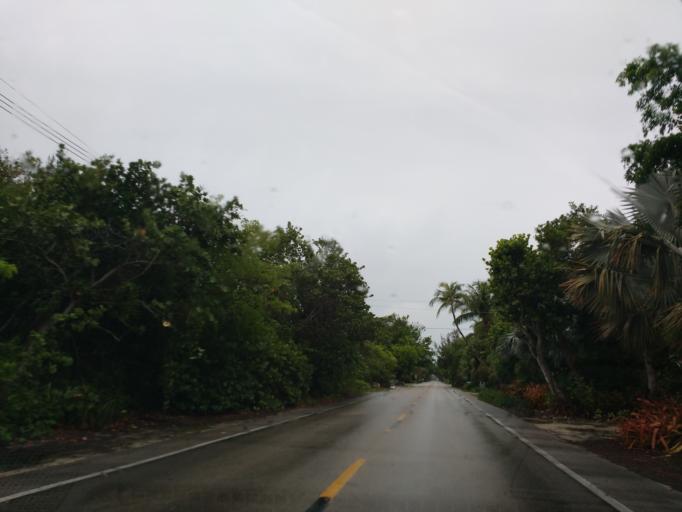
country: US
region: Florida
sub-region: Lee County
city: Saint James City
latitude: 26.4932
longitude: -82.1854
